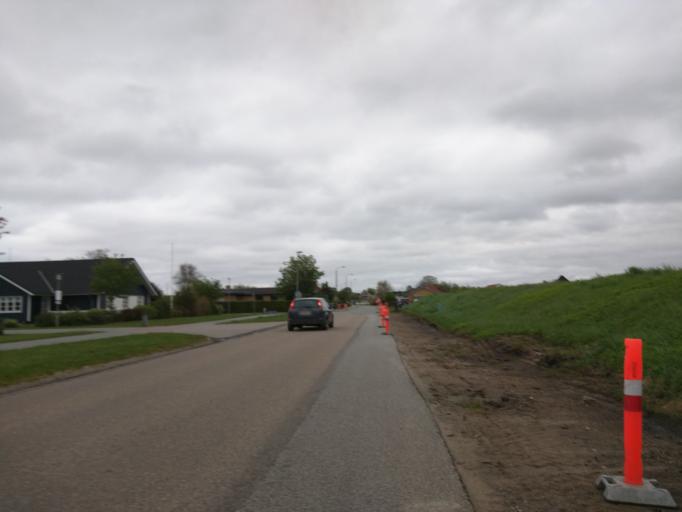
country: DK
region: Central Jutland
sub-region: Viborg Kommune
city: Viborg
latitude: 56.4330
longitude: 9.3800
